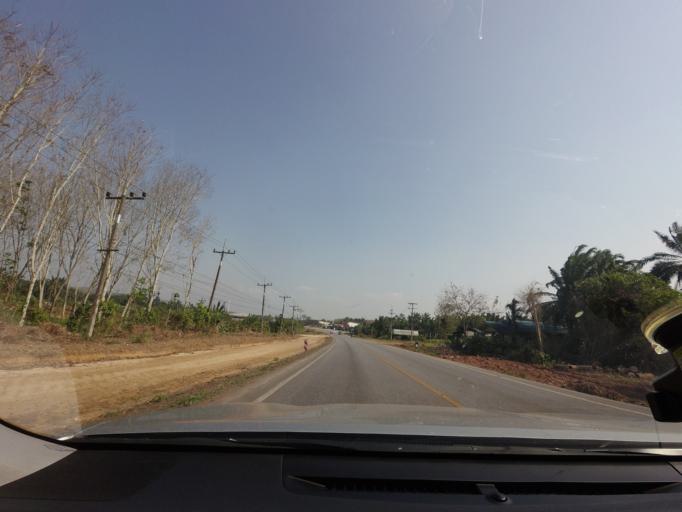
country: TH
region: Krabi
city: Plai Phraya
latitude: 8.6081
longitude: 99.0023
